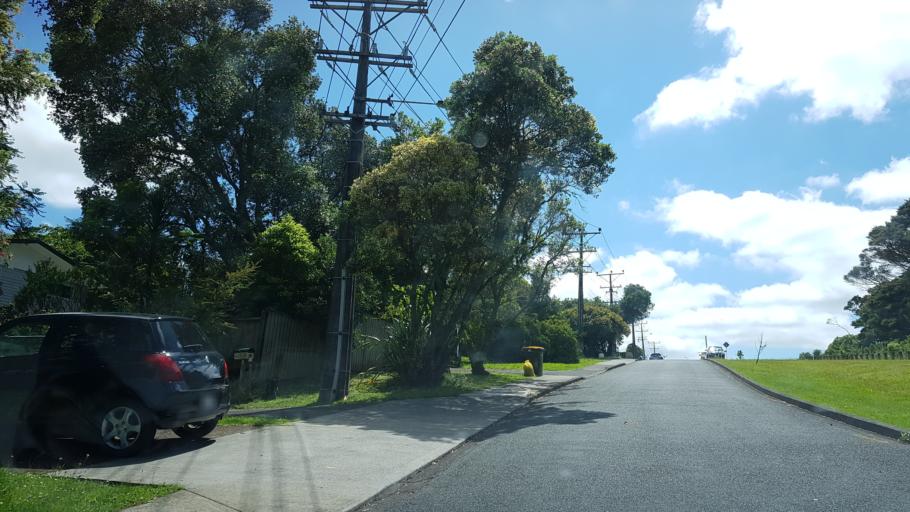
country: NZ
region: Auckland
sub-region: Auckland
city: North Shore
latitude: -36.7933
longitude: 174.7214
